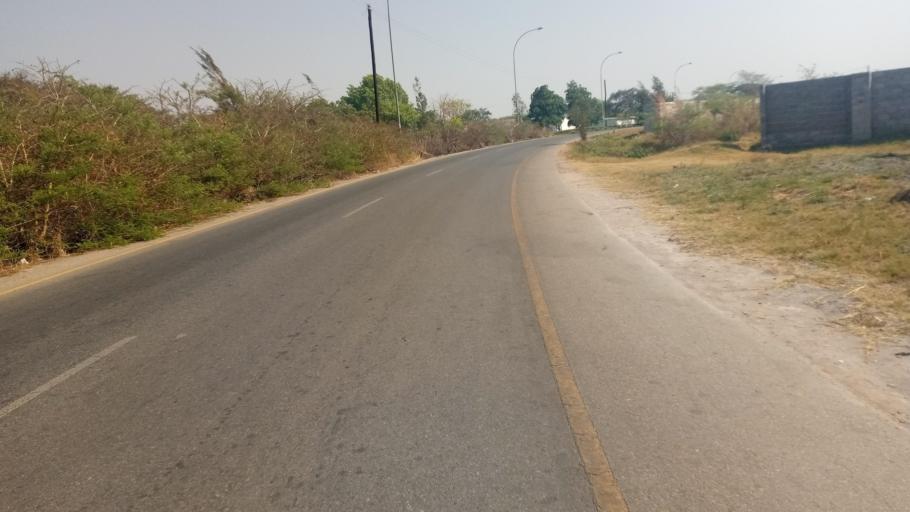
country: ZM
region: Lusaka
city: Lusaka
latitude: -15.4568
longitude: 28.4341
